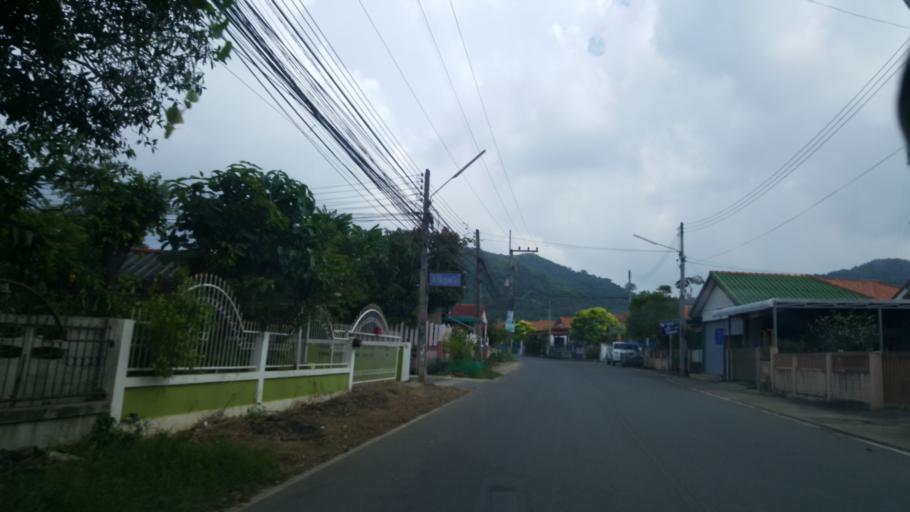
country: TH
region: Chon Buri
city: Sattahip
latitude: 12.6916
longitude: 100.9079
